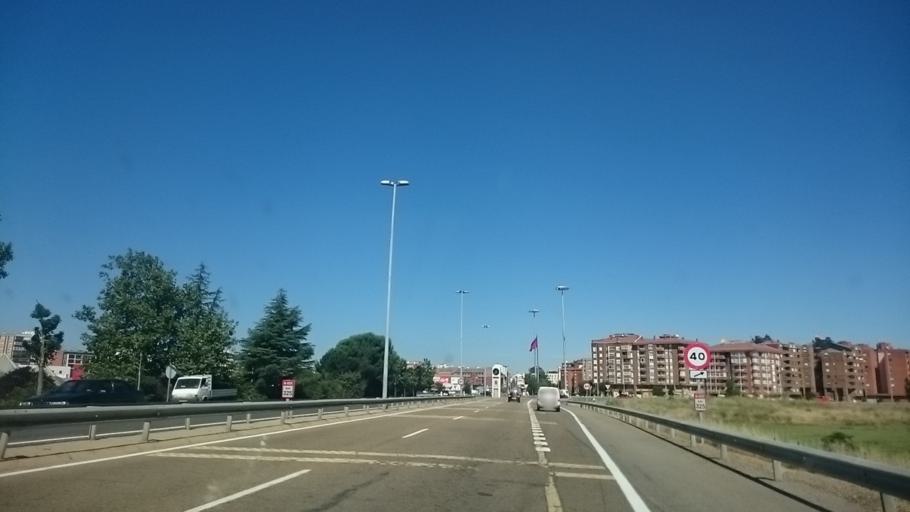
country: ES
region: Castille and Leon
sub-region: Provincia de Leon
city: Leon
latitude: 42.5870
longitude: -5.5540
